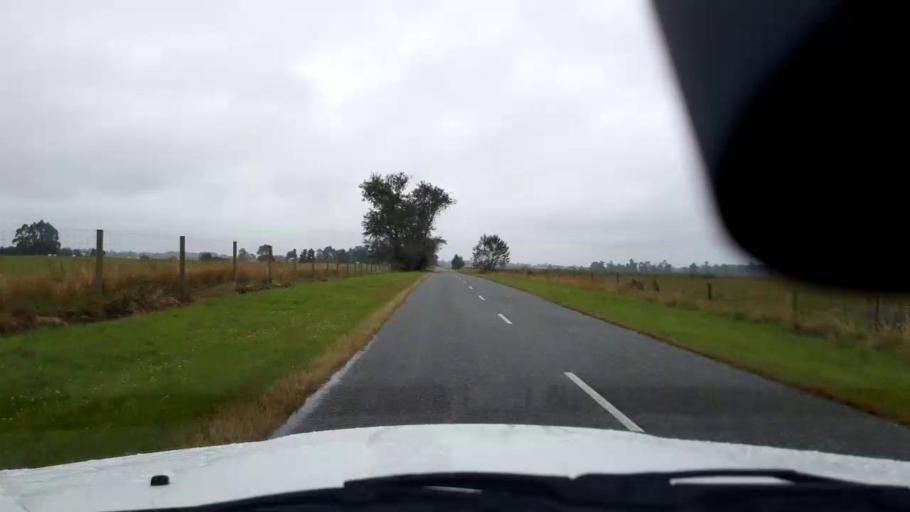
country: NZ
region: Canterbury
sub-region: Timaru District
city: Pleasant Point
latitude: -44.2518
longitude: 171.2224
